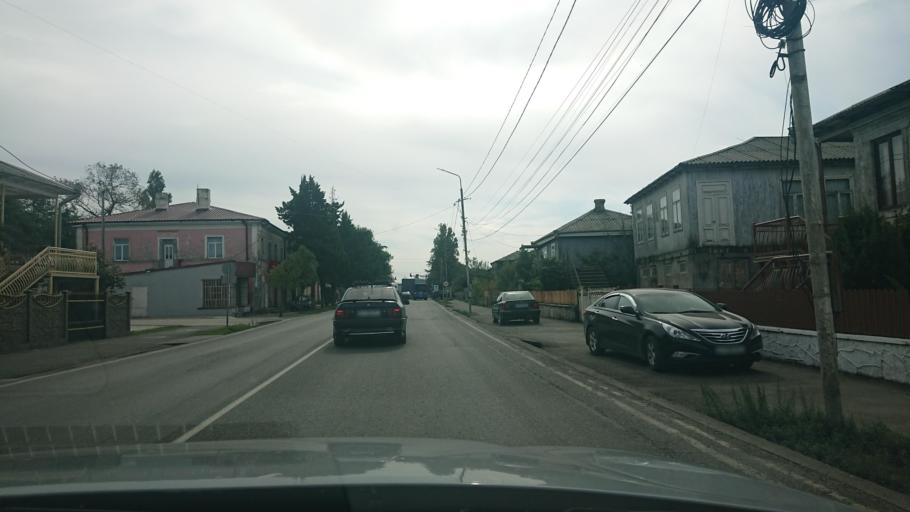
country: GE
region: Samegrelo and Zemo Svaneti
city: P'ot'i
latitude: 42.1574
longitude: 41.6693
